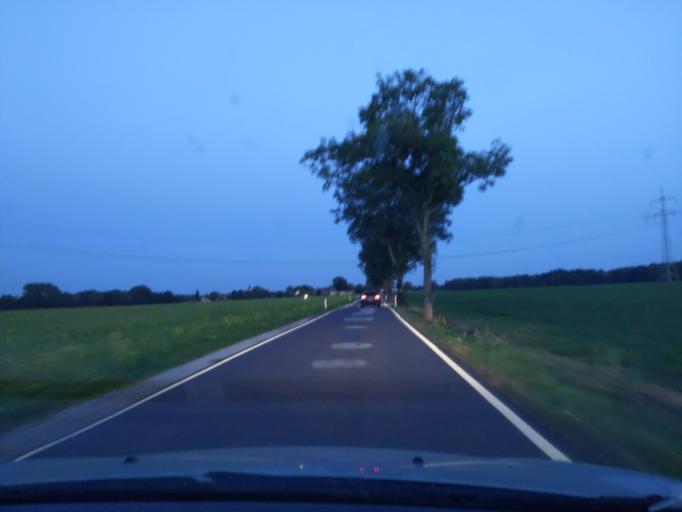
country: DE
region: Saxony
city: Grossdubrau
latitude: 51.3003
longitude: 14.4415
